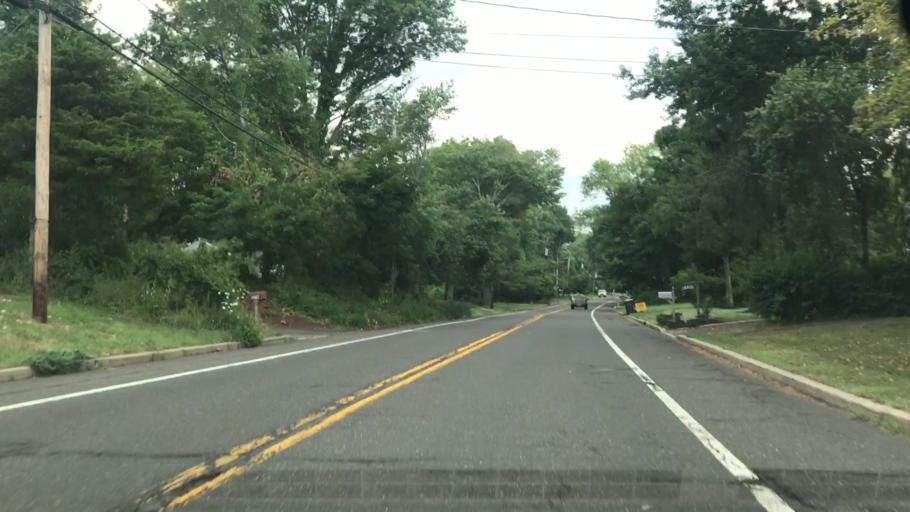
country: US
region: New Jersey
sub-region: Somerset County
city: Bradley Gardens
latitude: 40.5571
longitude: -74.6777
